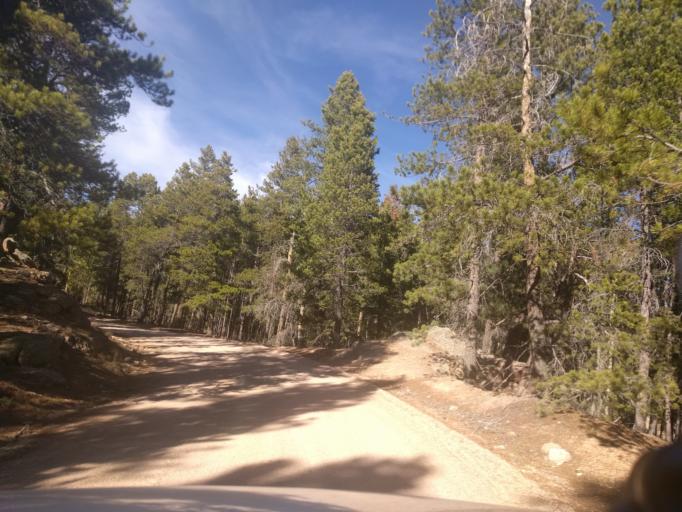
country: US
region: Colorado
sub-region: Douglas County
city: Perry Park
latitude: 39.2150
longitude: -105.0581
